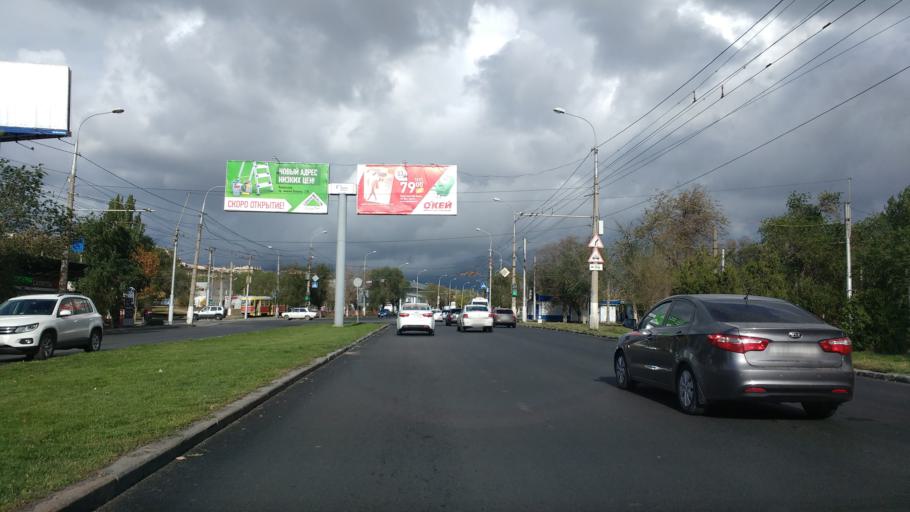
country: RU
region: Volgograd
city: Krasnoslobodsk
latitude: 48.7702
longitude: 44.5662
